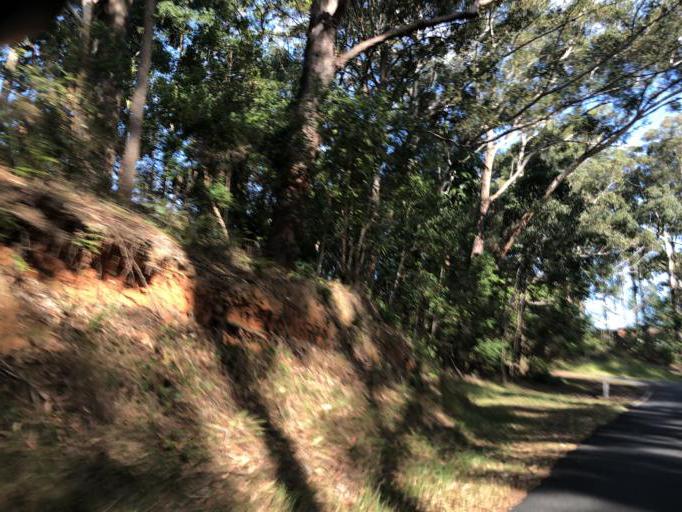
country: AU
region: New South Wales
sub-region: Coffs Harbour
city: Coffs Harbour
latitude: -30.2592
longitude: 153.1326
